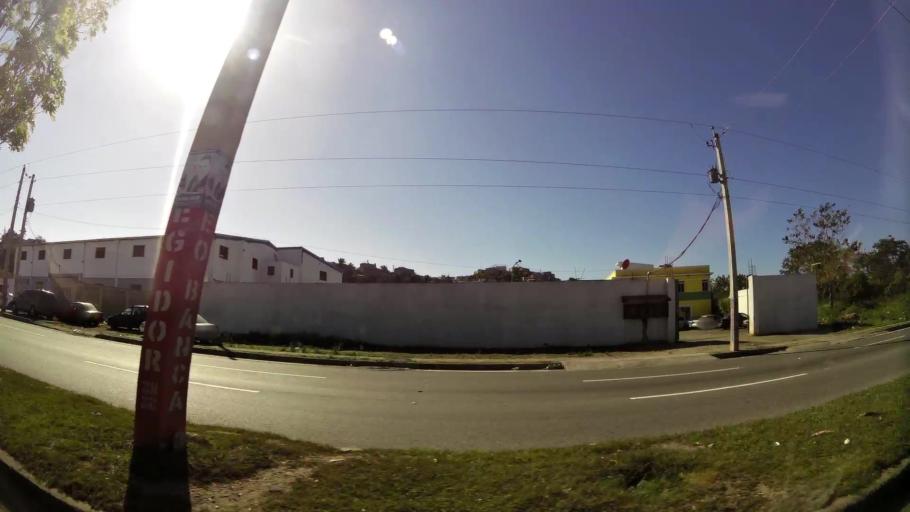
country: DO
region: San Cristobal
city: El Carril
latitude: 18.4482
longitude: -69.9944
